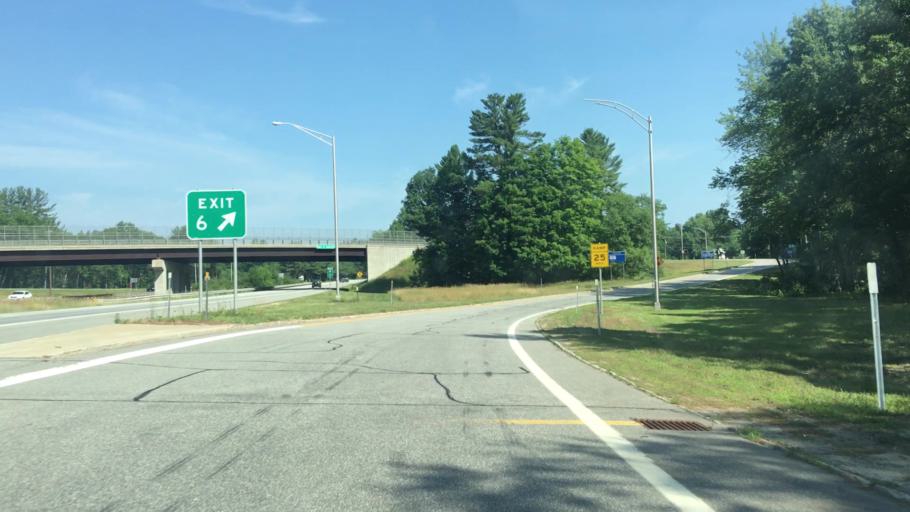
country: US
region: New Hampshire
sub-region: Merrimack County
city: Contoocook
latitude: 43.2019
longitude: -71.7066
